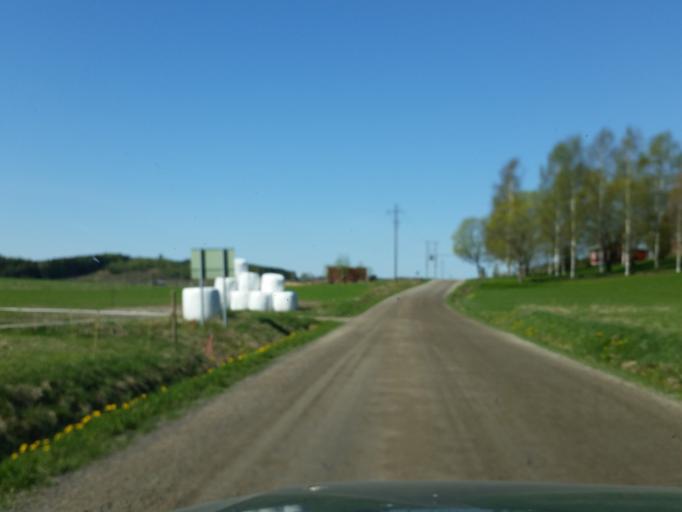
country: FI
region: Uusimaa
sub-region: Helsinki
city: Karjalohja
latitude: 60.1406
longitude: 23.7431
